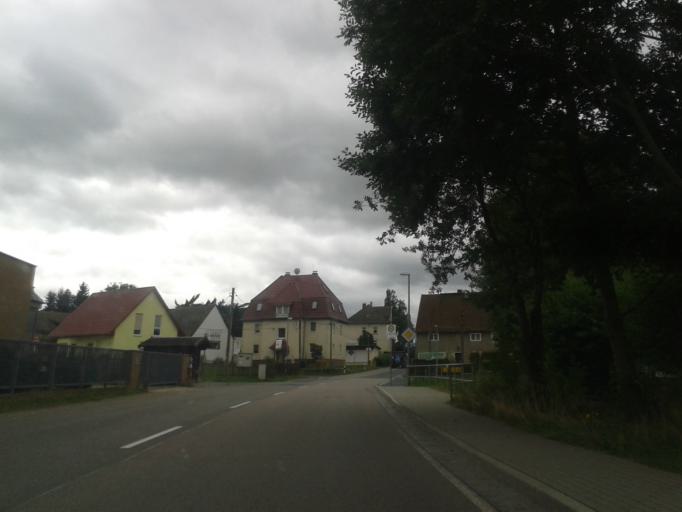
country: DE
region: Saxony
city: Wilsdruff
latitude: 51.0192
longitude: 13.5592
